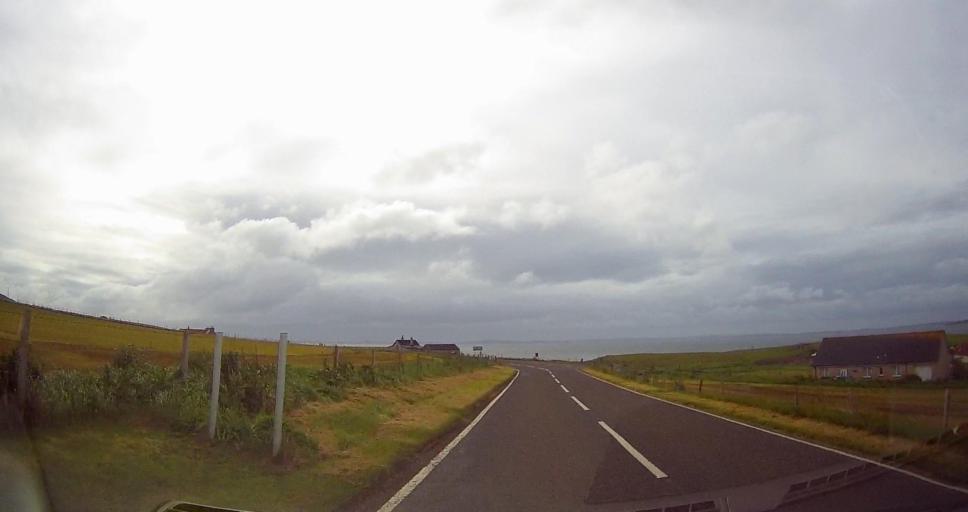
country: GB
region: Scotland
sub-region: Orkney Islands
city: Stromness
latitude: 58.9201
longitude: -3.1830
